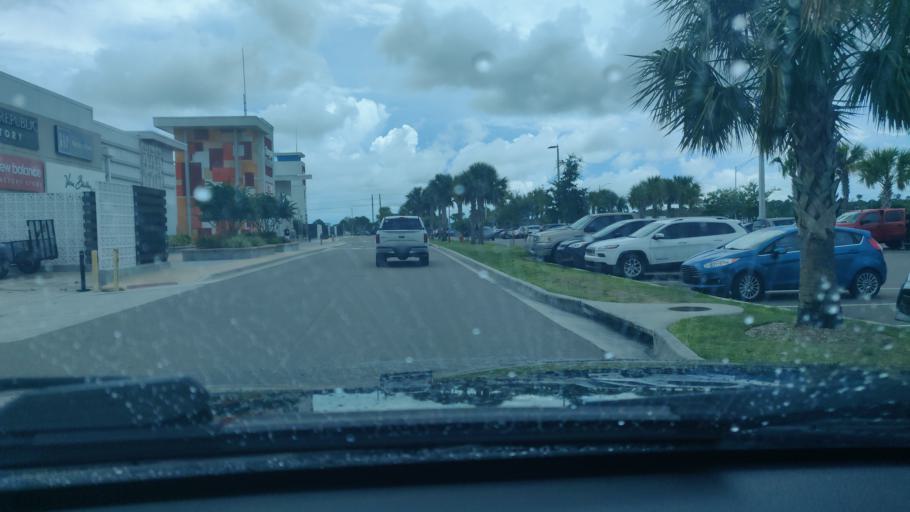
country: US
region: Florida
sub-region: Volusia County
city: Holly Hill
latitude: 29.2140
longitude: -81.1000
